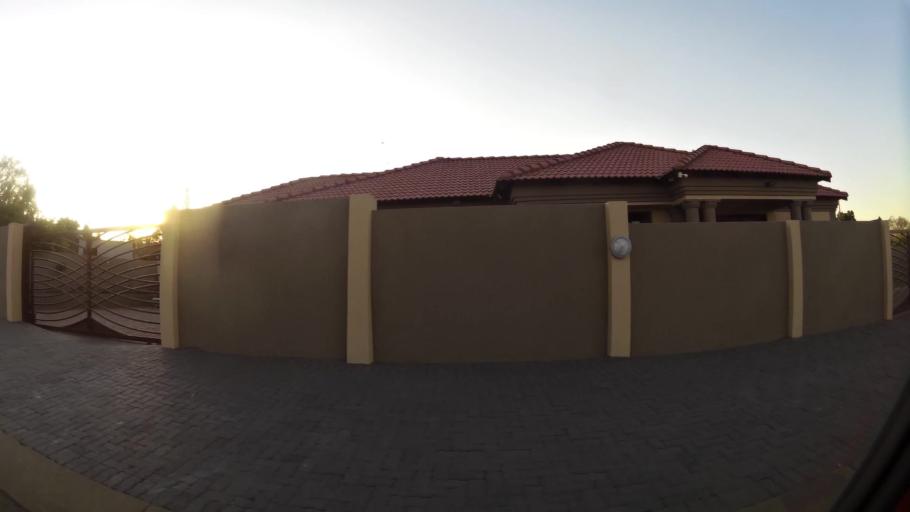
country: ZA
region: North-West
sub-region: Bojanala Platinum District Municipality
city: Rustenburg
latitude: -25.6357
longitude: 27.2058
